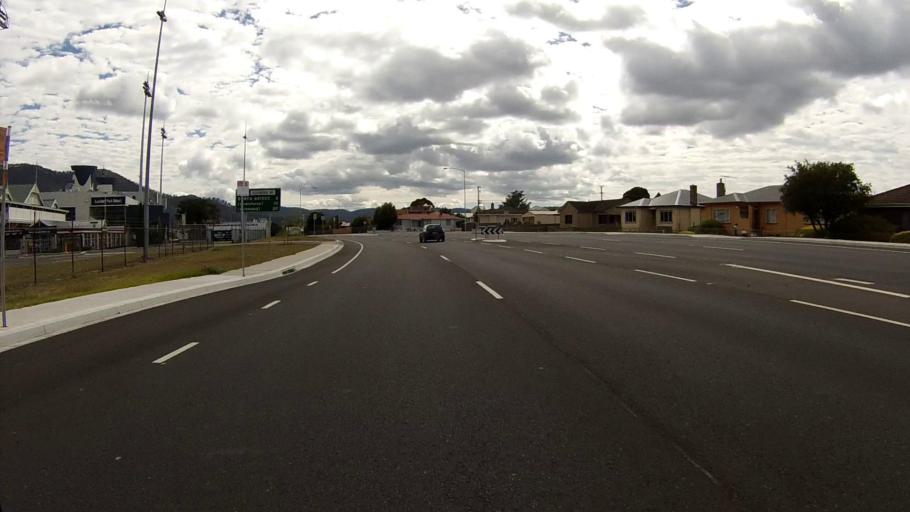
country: AU
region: Tasmania
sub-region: Glenorchy
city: Goodwood
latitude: -42.8267
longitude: 147.2878
